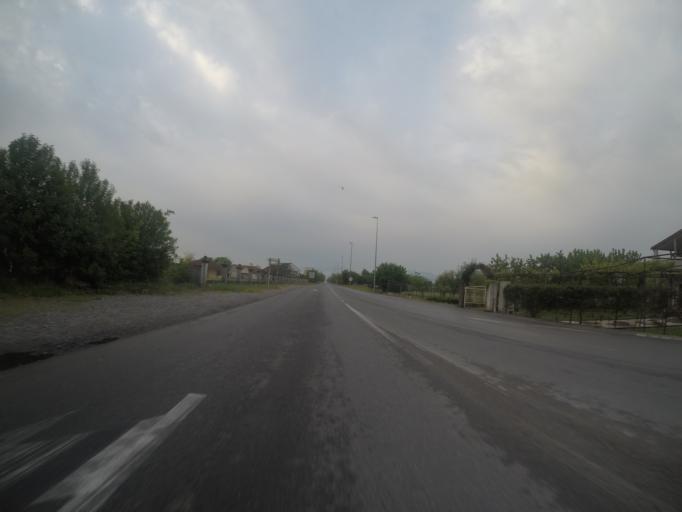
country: ME
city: Mojanovici
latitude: 42.3437
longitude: 19.2219
